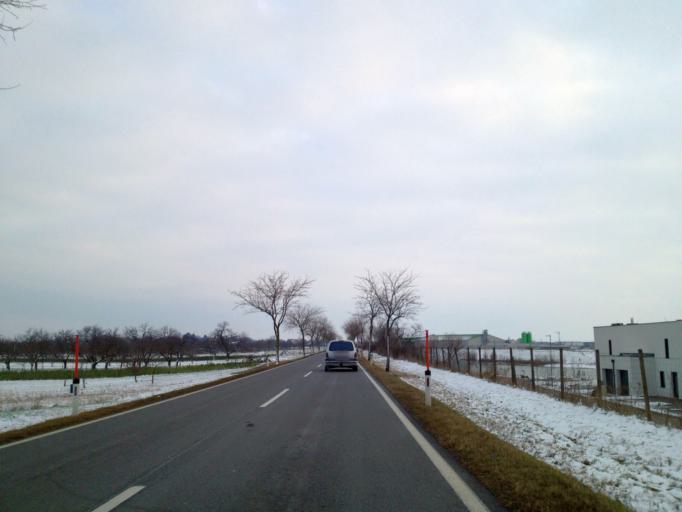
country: AT
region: Lower Austria
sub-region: Politischer Bezirk Bruck an der Leitha
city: Berg
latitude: 48.1002
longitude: 17.0462
